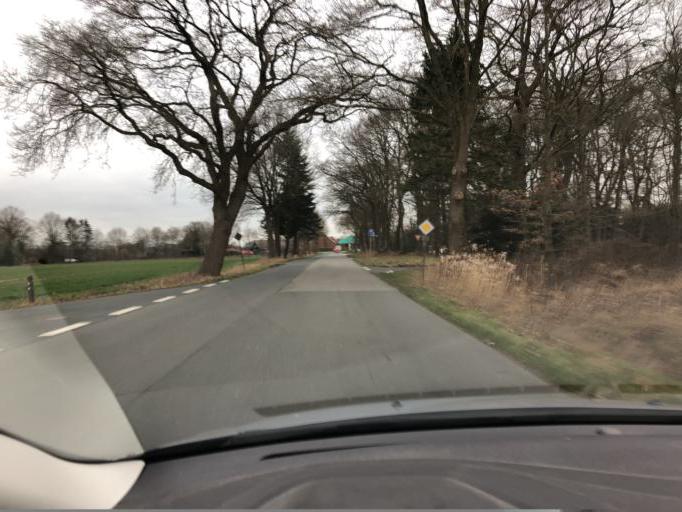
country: DE
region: Lower Saxony
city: Bad Zwischenahn
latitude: 53.1791
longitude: 8.0565
